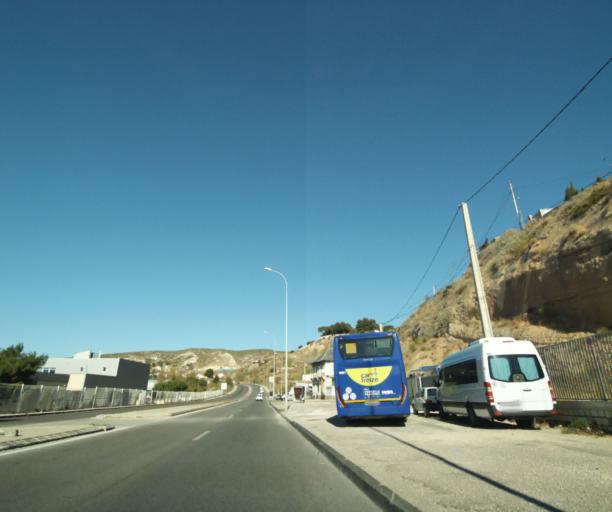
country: FR
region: Provence-Alpes-Cote d'Azur
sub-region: Departement des Bouches-du-Rhone
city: Marseille 16
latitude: 43.3548
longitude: 5.3279
